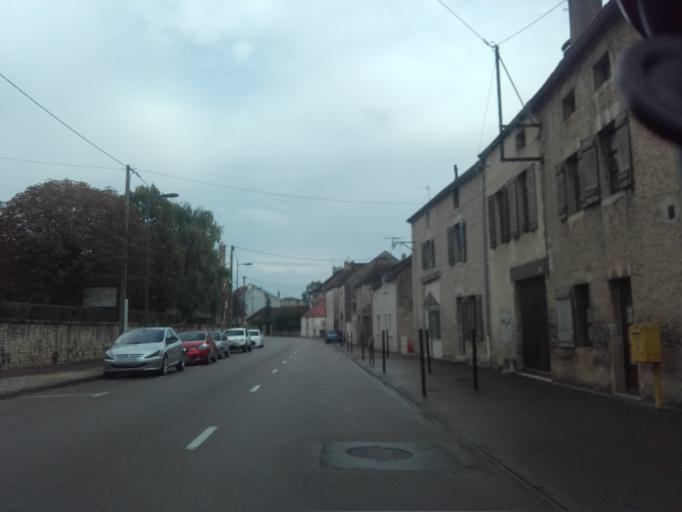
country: FR
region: Bourgogne
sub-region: Departement de la Cote-d'Or
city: Beaune
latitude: 47.0242
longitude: 4.8292
